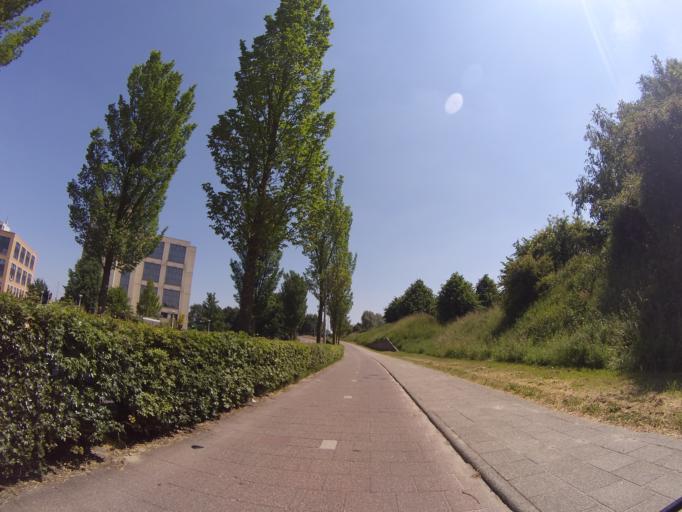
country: NL
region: Utrecht
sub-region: Gemeente Amersfoort
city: Hoogland
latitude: 52.1872
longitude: 5.4082
